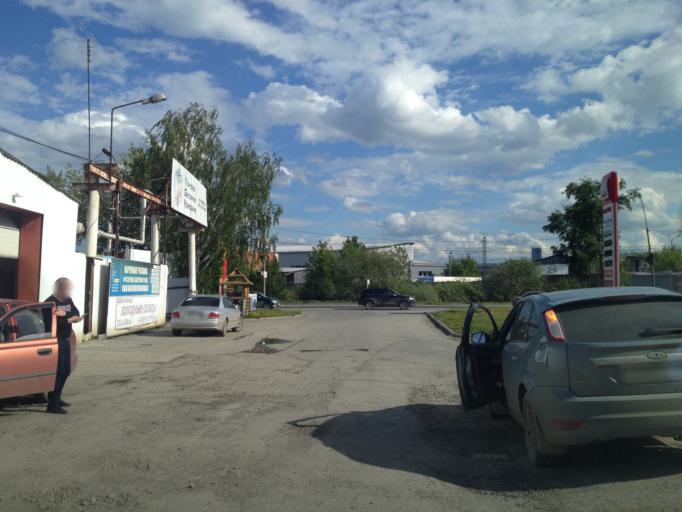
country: RU
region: Sverdlovsk
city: Yekaterinburg
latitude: 56.8691
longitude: 60.5858
